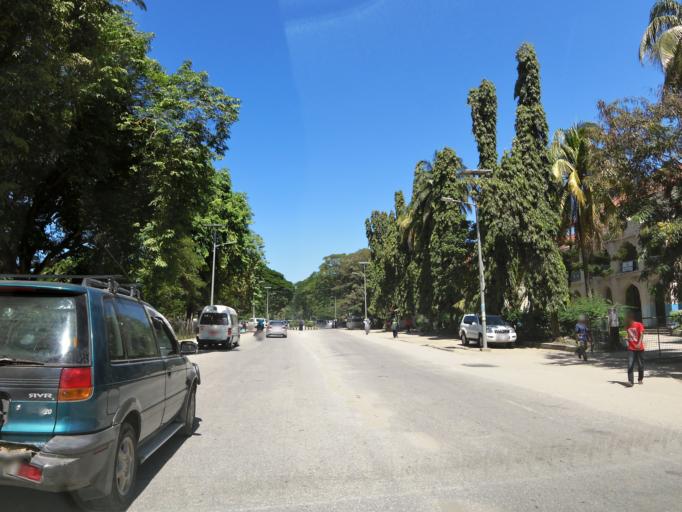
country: TZ
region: Zanzibar Urban/West
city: Zanzibar
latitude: -6.1650
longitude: 39.1928
